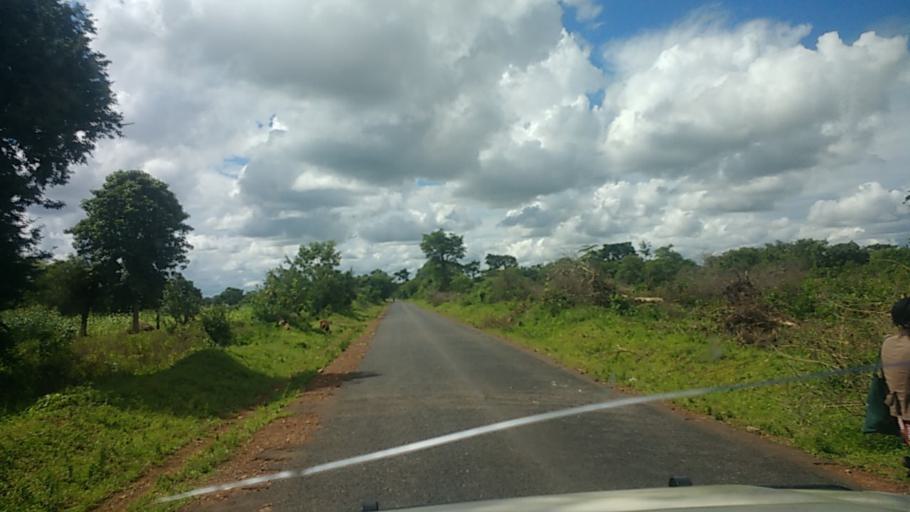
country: UG
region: Eastern Region
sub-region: Katakwi District
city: Katakwi
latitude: 1.8901
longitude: 33.9590
